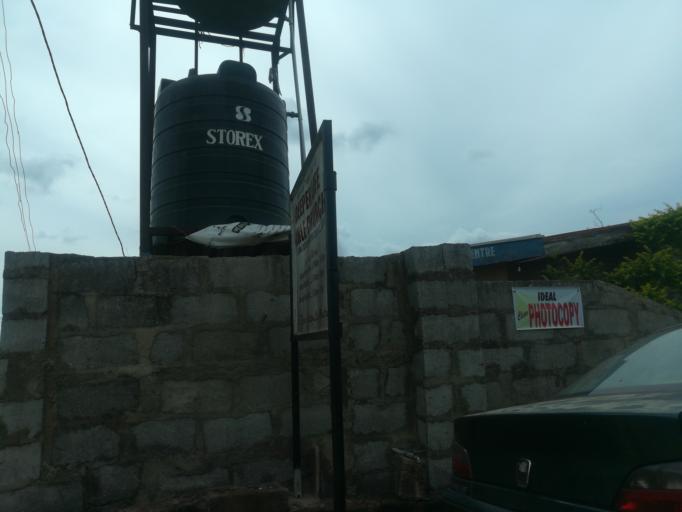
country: NG
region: Oyo
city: Ibadan
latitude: 7.3655
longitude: 3.9710
